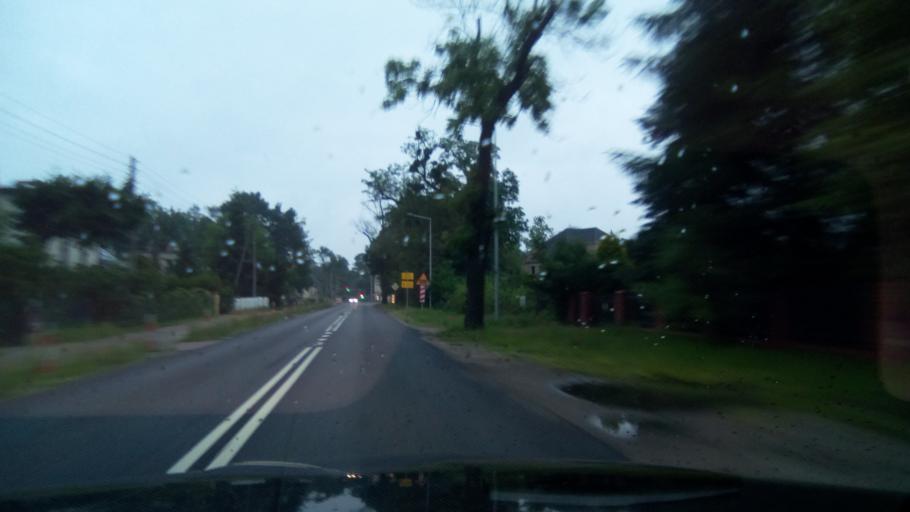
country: PL
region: Greater Poland Voivodeship
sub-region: Powiat poznanski
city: Kobylnica
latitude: 52.4432
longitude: 17.0759
